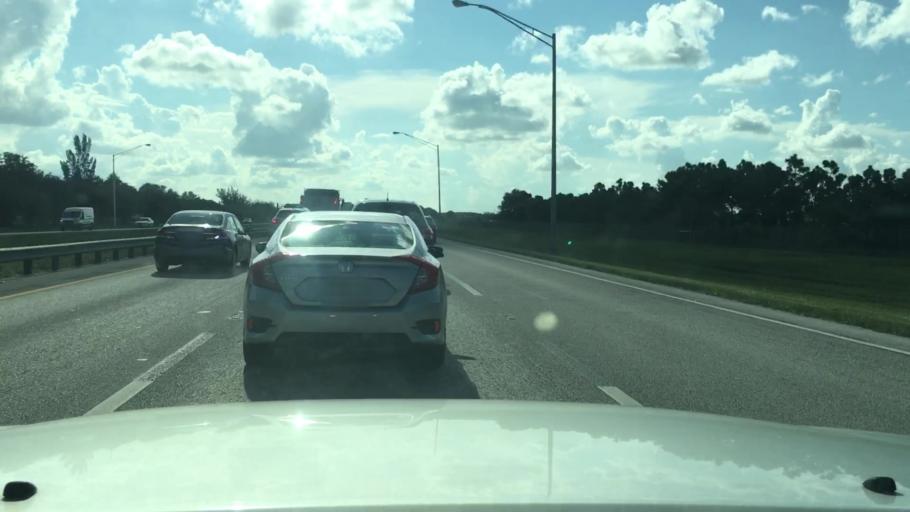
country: US
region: Florida
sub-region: Miami-Dade County
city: Lake Lucerne
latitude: 25.9732
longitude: -80.2540
